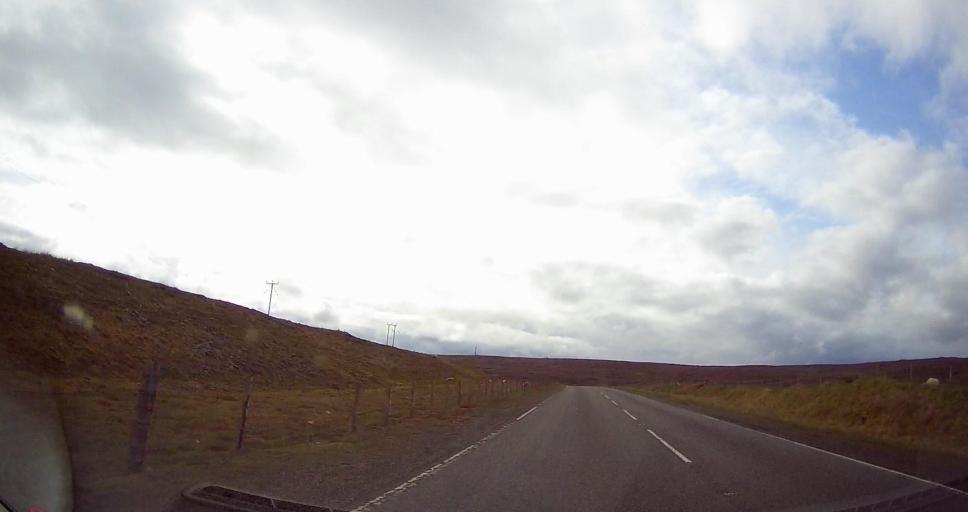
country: GB
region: Scotland
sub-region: Shetland Islands
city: Lerwick
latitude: 60.4426
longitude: -1.2333
